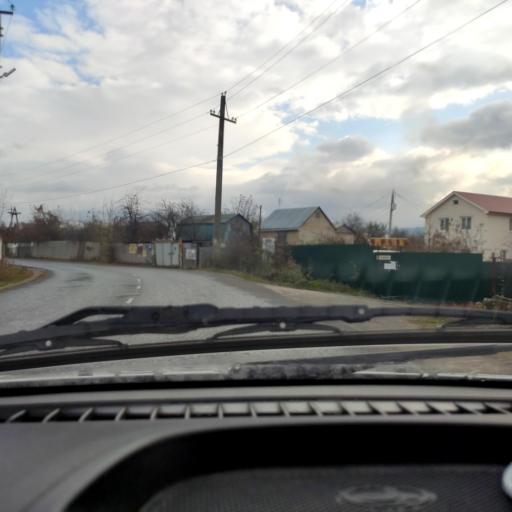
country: RU
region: Samara
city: Zhigulevsk
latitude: 53.4661
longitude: 49.6402
